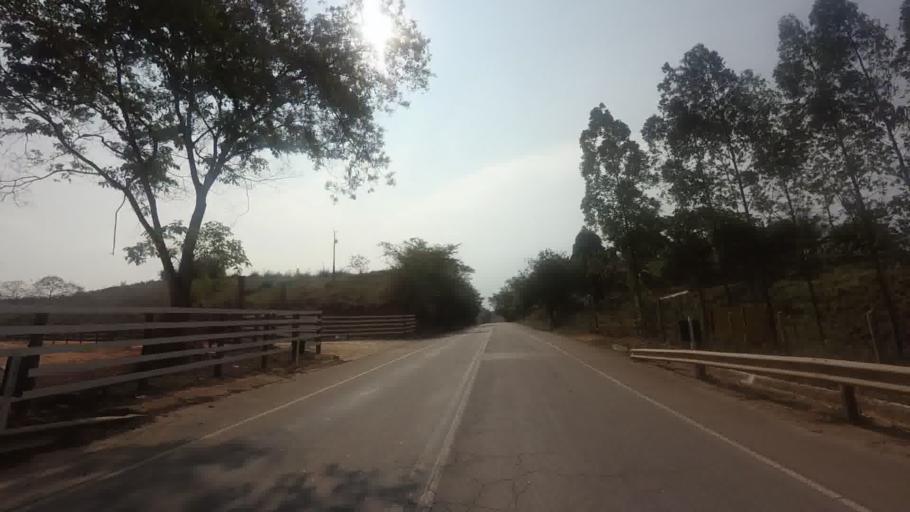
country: BR
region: Rio de Janeiro
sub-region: Bom Jesus Do Itabapoana
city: Bom Jesus do Itabapoana
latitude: -21.1347
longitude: -41.6429
